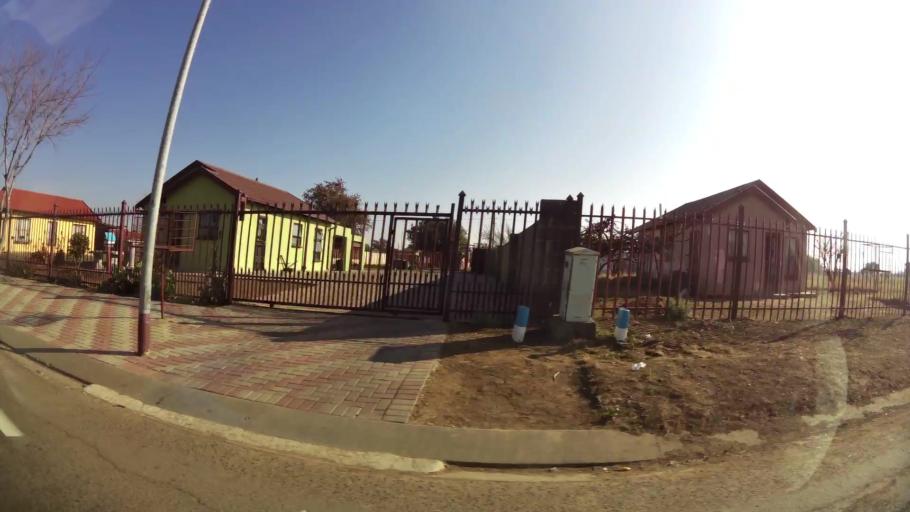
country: ZA
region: Orange Free State
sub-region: Mangaung Metropolitan Municipality
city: Bloemfontein
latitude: -29.1862
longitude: 26.1764
